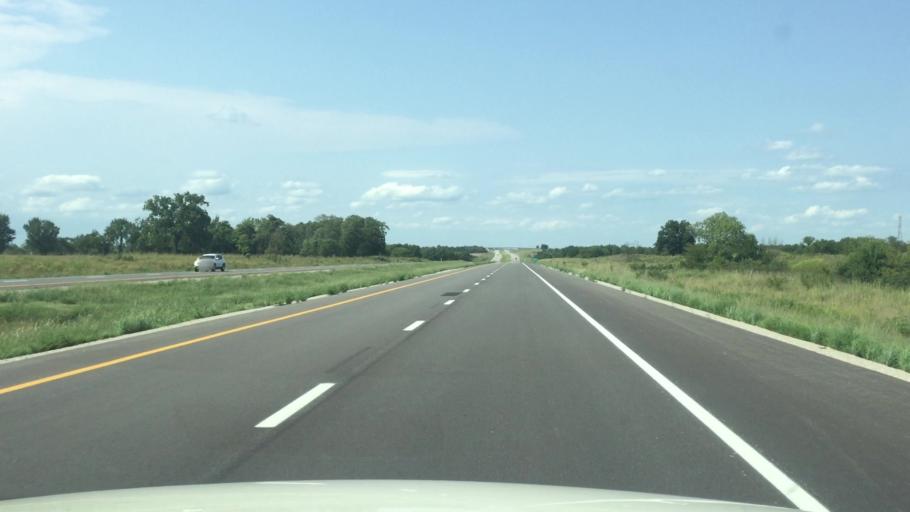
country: US
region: Kansas
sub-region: Linn County
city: La Cygne
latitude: 38.3780
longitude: -94.6874
